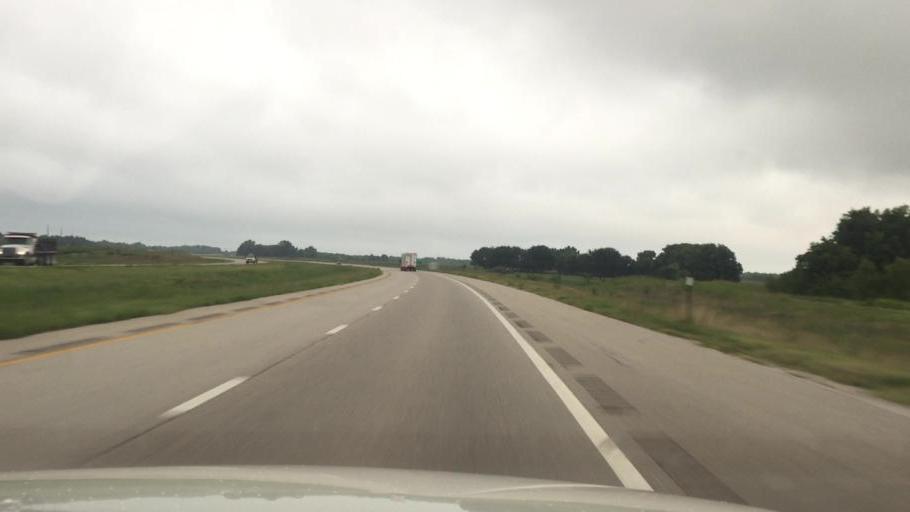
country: US
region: Kansas
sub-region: Montgomery County
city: Coffeyville
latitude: 37.0798
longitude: -95.5899
